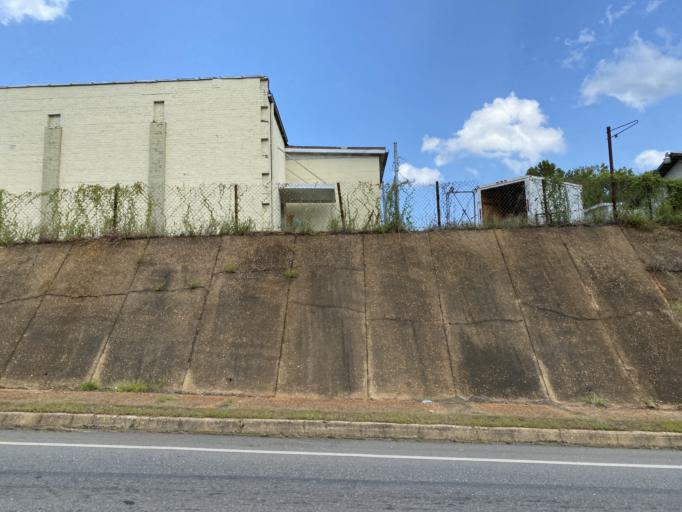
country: US
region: Alabama
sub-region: Wilcox County
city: Camden
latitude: 31.9914
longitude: -87.2882
